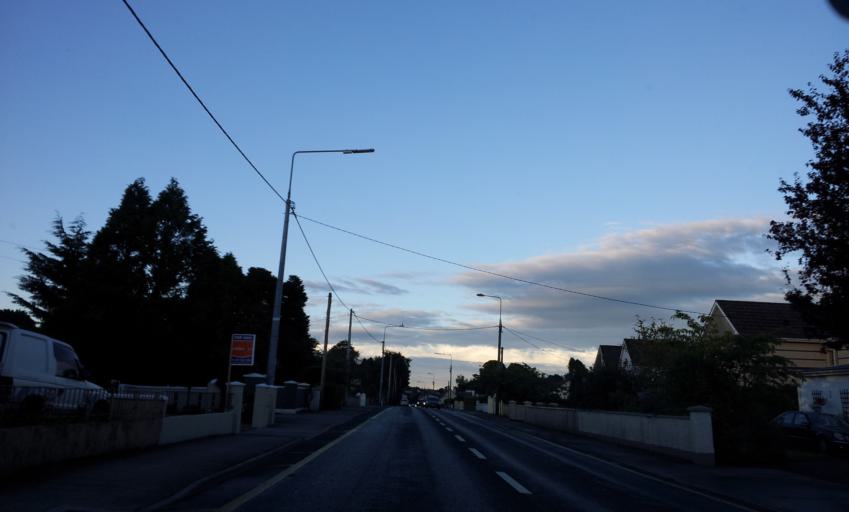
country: IE
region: Munster
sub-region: County Limerick
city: Newcastle West
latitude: 52.4465
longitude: -9.0691
